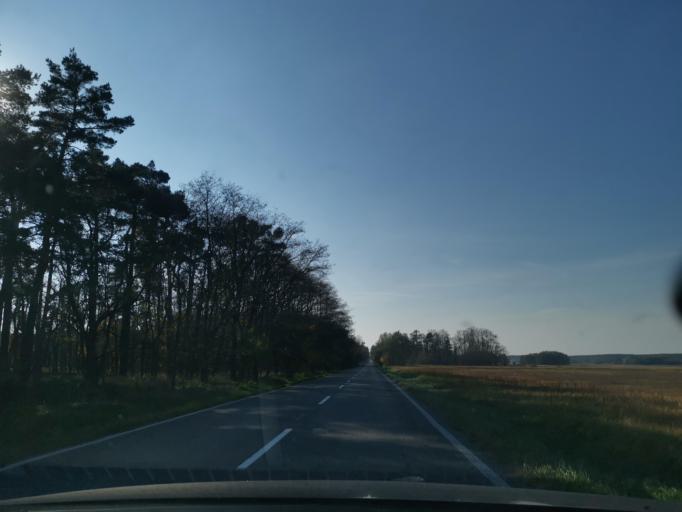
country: SK
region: Trnavsky
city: Gbely
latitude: 48.5724
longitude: 17.1624
